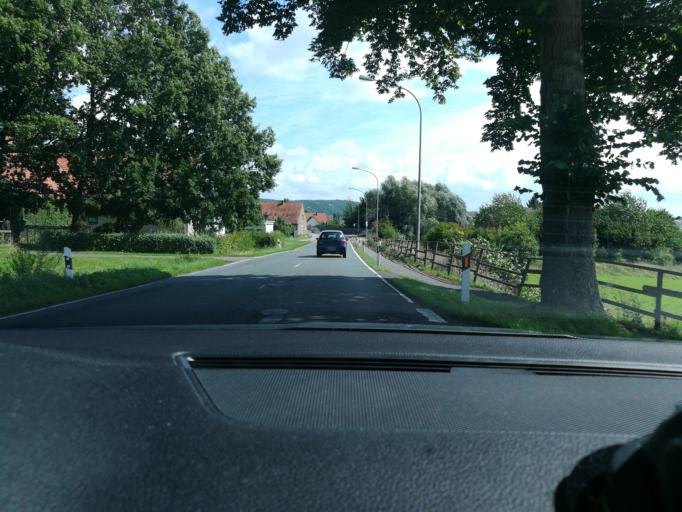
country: DE
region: North Rhine-Westphalia
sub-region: Regierungsbezirk Detmold
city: Huellhorst
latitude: 52.2875
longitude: 8.6529
